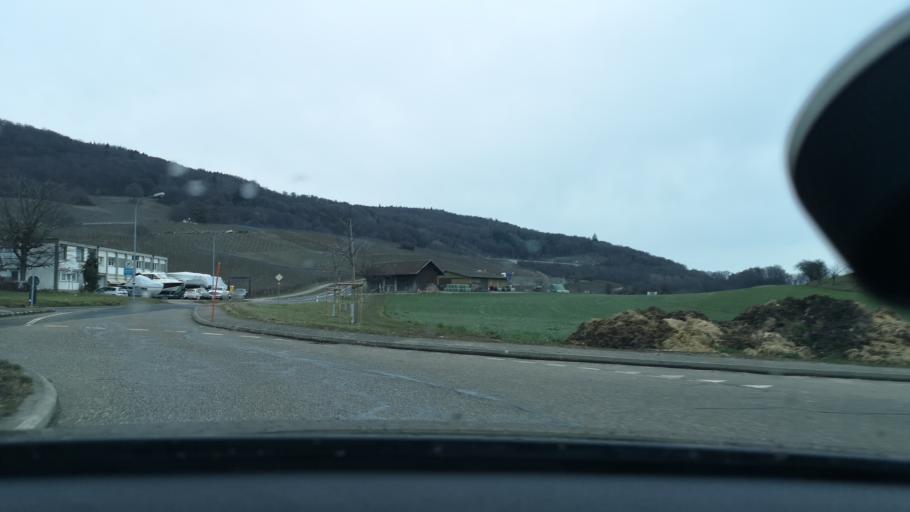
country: CH
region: Vaud
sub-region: Jura-Nord vaudois District
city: Yvonand
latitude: 46.8542
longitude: 6.7230
